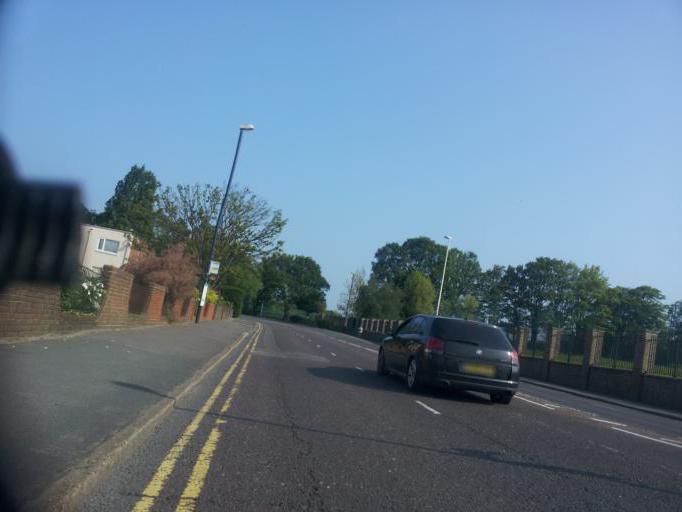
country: GB
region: England
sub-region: Kent
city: Gillingham
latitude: 51.3909
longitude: 0.5368
